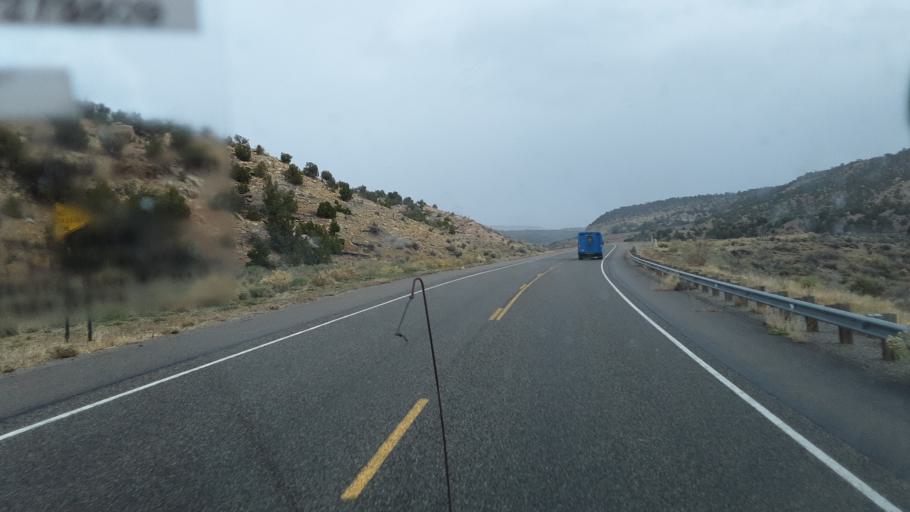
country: US
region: New Mexico
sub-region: Rio Arriba County
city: Santa Teresa
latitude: 36.3736
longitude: -106.5051
